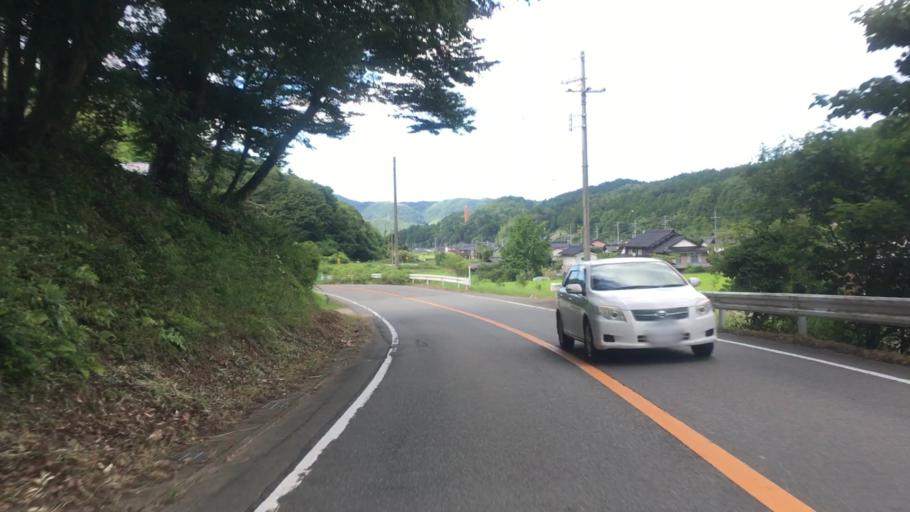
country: JP
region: Hyogo
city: Toyooka
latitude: 35.5327
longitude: 134.7886
